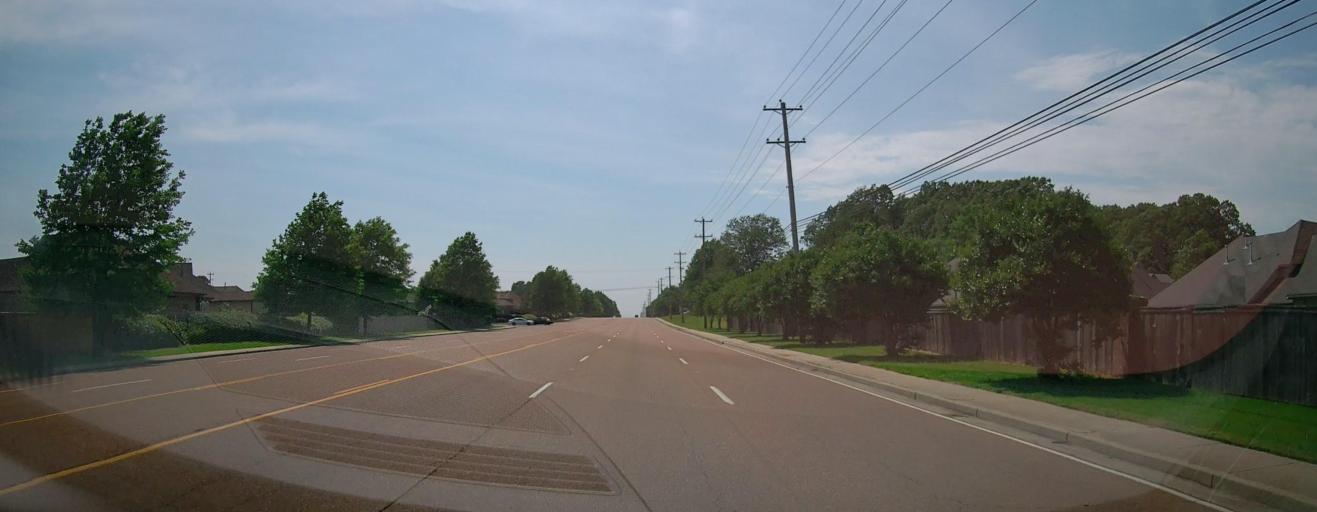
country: US
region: Mississippi
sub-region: De Soto County
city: Olive Branch
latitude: 35.0205
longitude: -89.8098
